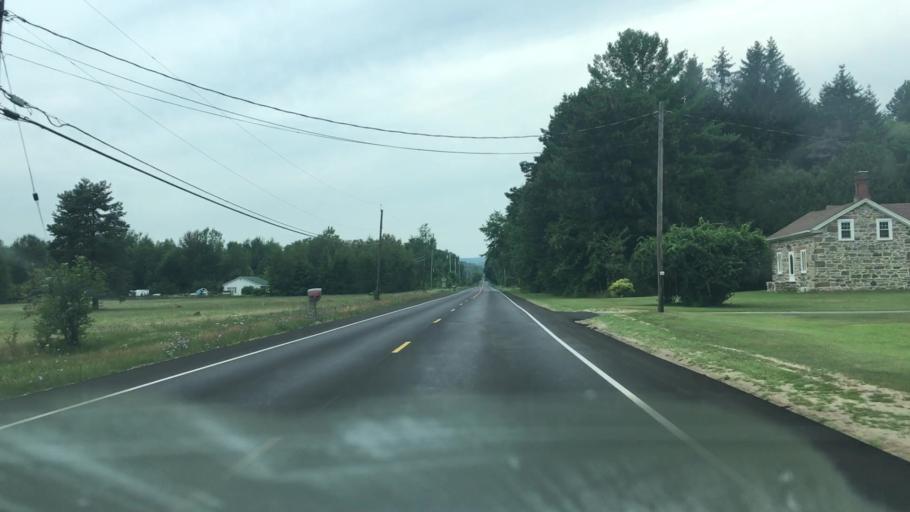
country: US
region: New York
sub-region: Clinton County
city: Plattsburgh West
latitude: 44.6517
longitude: -73.5259
